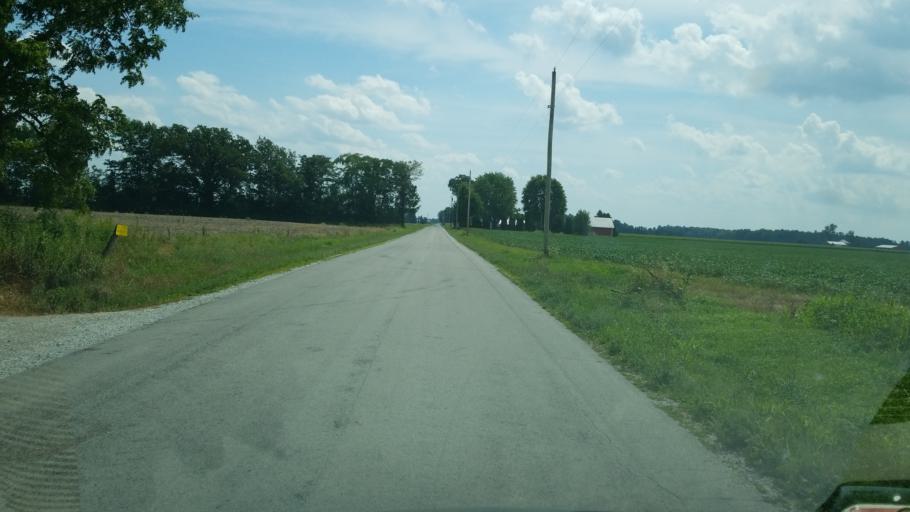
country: US
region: Ohio
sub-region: Wyandot County
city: Carey
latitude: 40.8980
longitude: -83.4623
